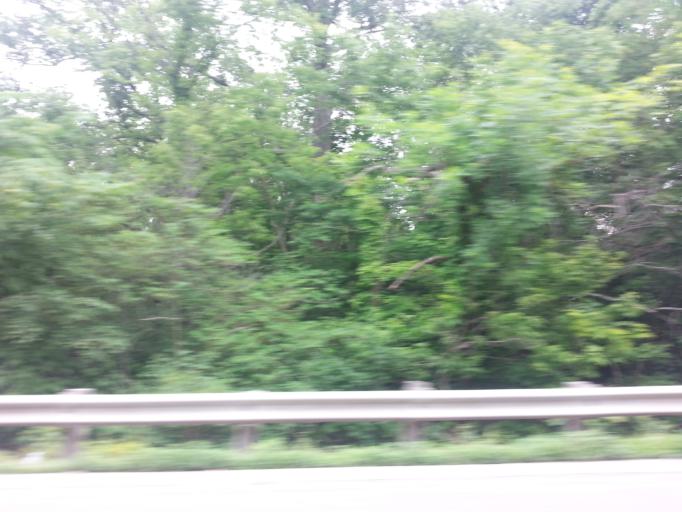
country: US
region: Ohio
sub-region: Brown County
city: Mount Orab
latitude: 39.0157
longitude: -83.9243
